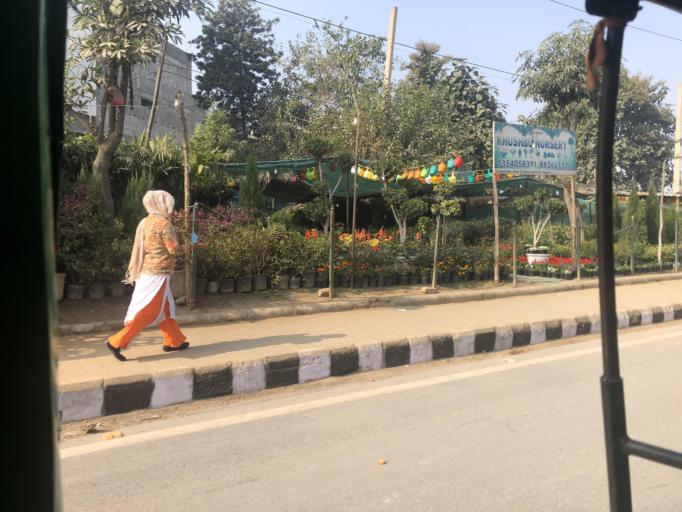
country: IN
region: Haryana
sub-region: Gurgaon
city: Gurgaon
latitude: 28.4368
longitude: 77.0901
